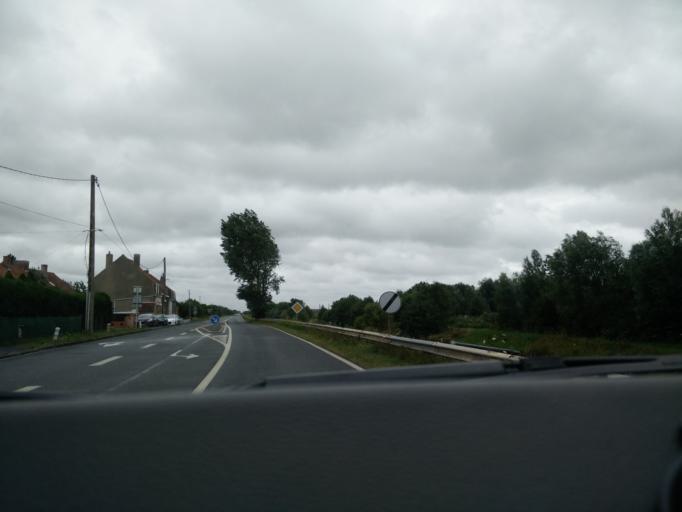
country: FR
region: Nord-Pas-de-Calais
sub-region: Departement du Nord
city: Zuydcoote
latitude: 51.0590
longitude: 2.4943
